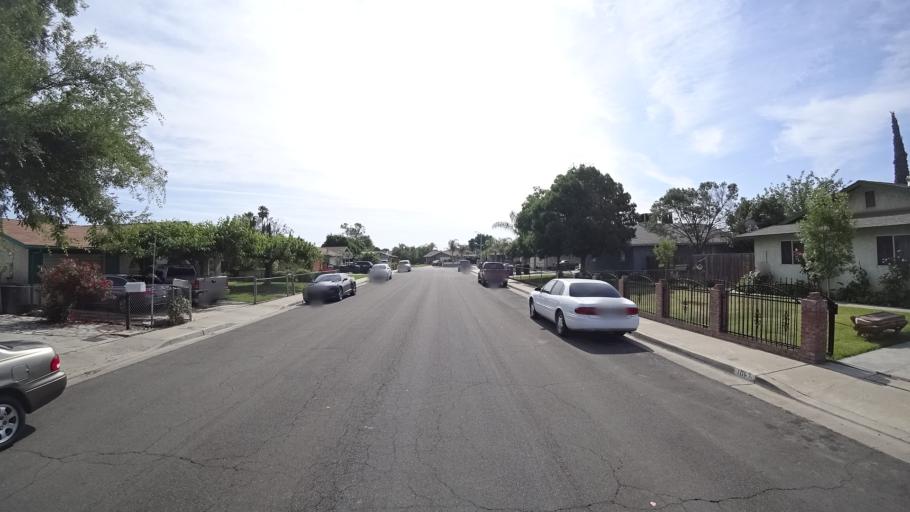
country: US
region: California
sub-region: Kings County
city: Hanford
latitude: 36.3101
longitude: -119.6609
